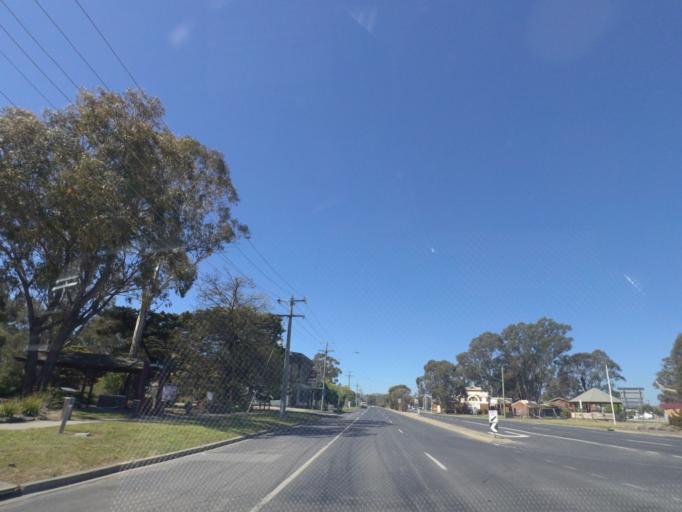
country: AU
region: Victoria
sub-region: Murrindindi
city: Kinglake West
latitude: -37.0194
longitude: 145.1288
